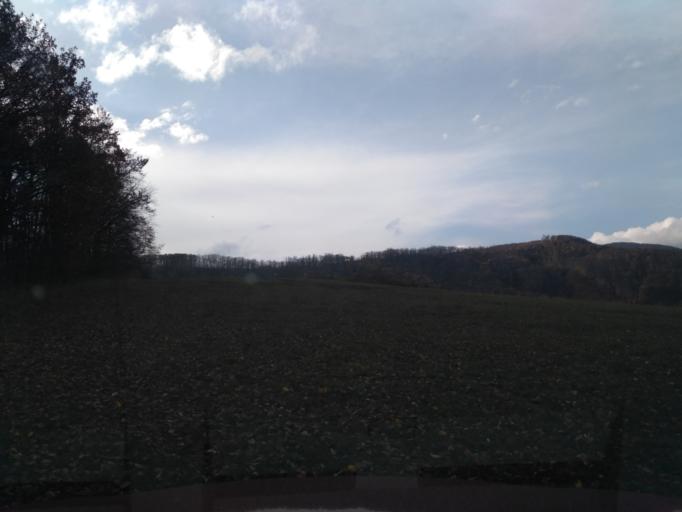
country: SK
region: Presovsky
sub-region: Okres Presov
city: Presov
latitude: 48.8726
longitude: 21.2323
